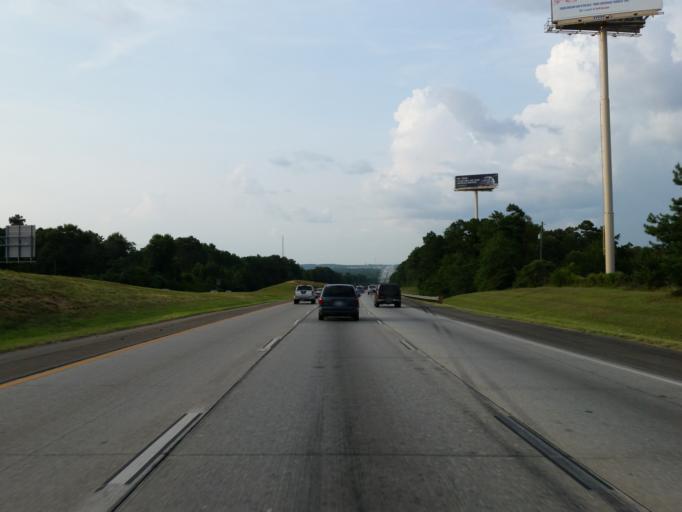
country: US
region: Georgia
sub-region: Peach County
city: Byron
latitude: 32.6750
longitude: -83.7441
